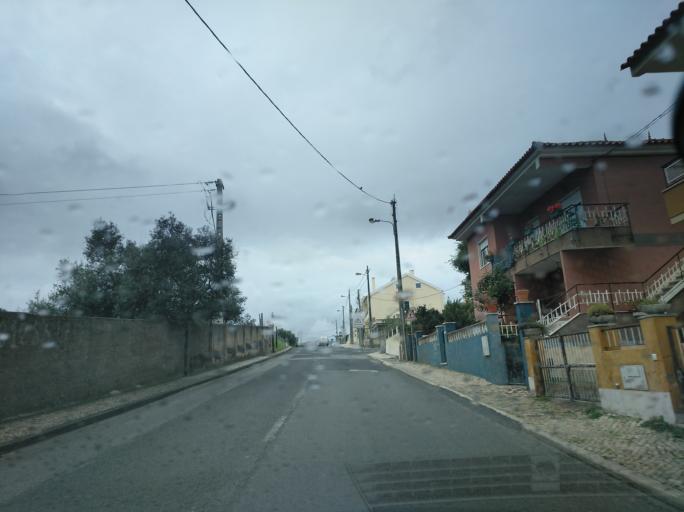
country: PT
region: Lisbon
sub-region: Odivelas
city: Famoes
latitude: 38.7910
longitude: -9.2002
